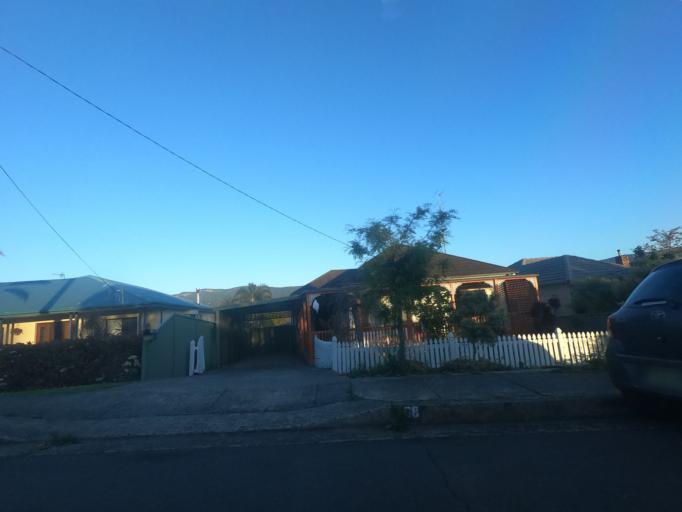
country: AU
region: New South Wales
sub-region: Wollongong
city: Dapto
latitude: -34.5031
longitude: 150.7870
